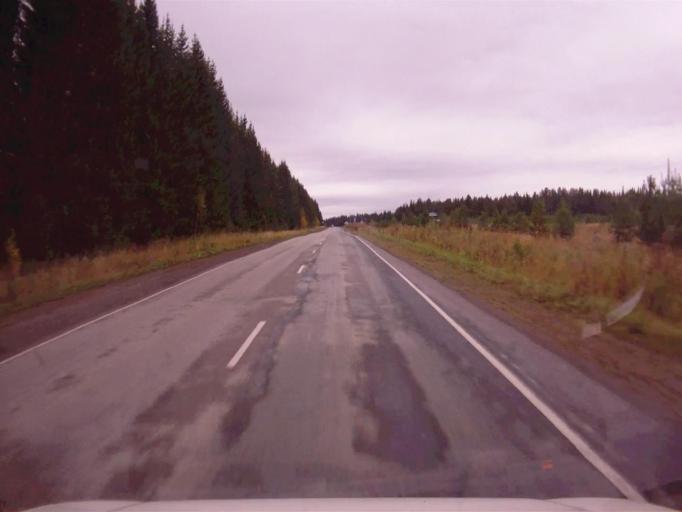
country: RU
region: Chelyabinsk
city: Nyazepetrovsk
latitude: 56.0657
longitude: 59.6559
